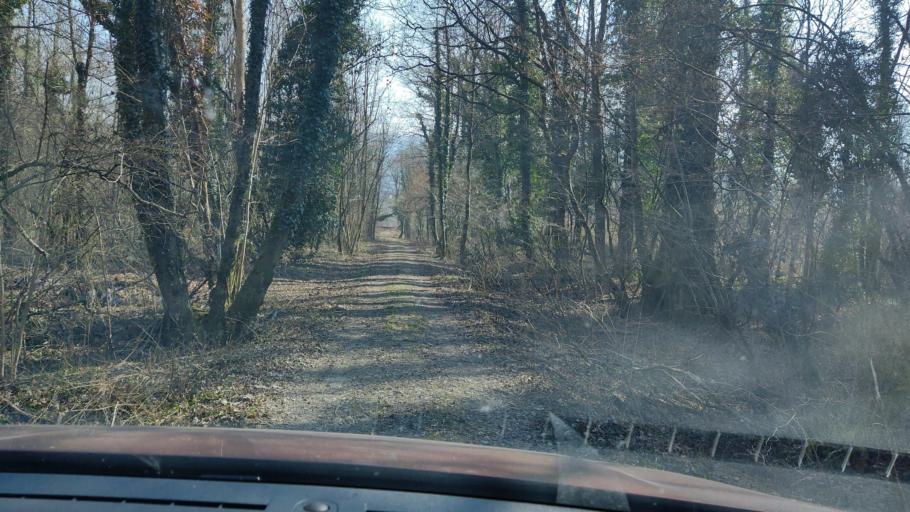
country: FR
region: Rhone-Alpes
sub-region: Departement de la Savoie
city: Cruet
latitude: 45.5113
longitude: 6.0840
